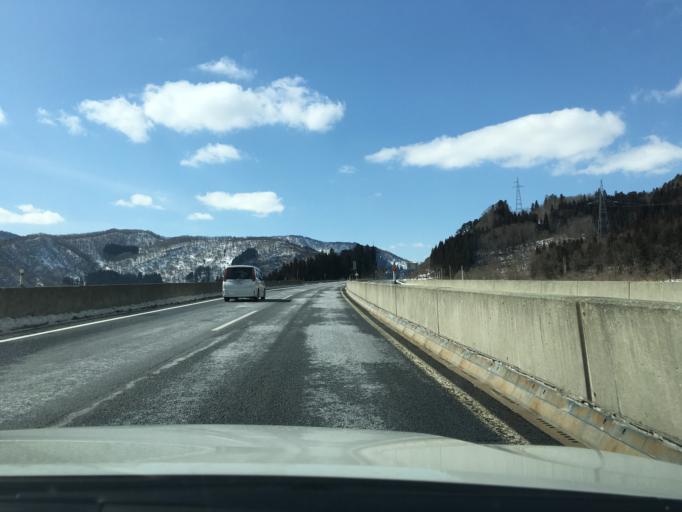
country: JP
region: Yamagata
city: Sagae
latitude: 38.4372
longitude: 140.0849
